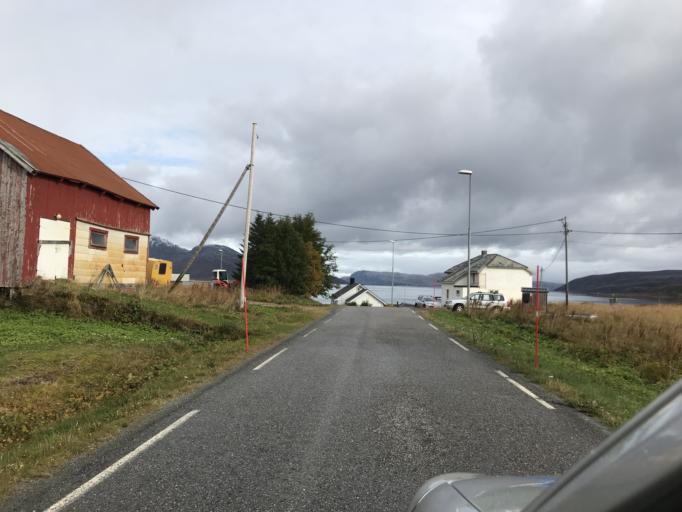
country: NO
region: Troms
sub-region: Tromso
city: Tromso
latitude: 70.0755
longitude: 18.9808
